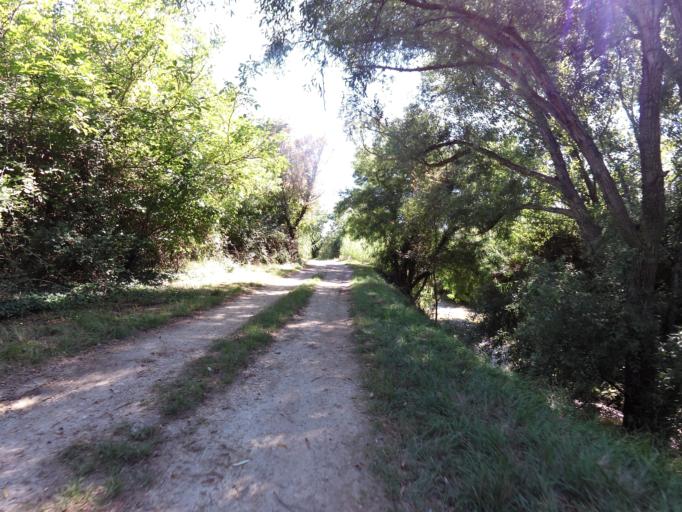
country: FR
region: Languedoc-Roussillon
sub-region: Departement du Gard
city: Vergeze
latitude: 43.7416
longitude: 4.2129
